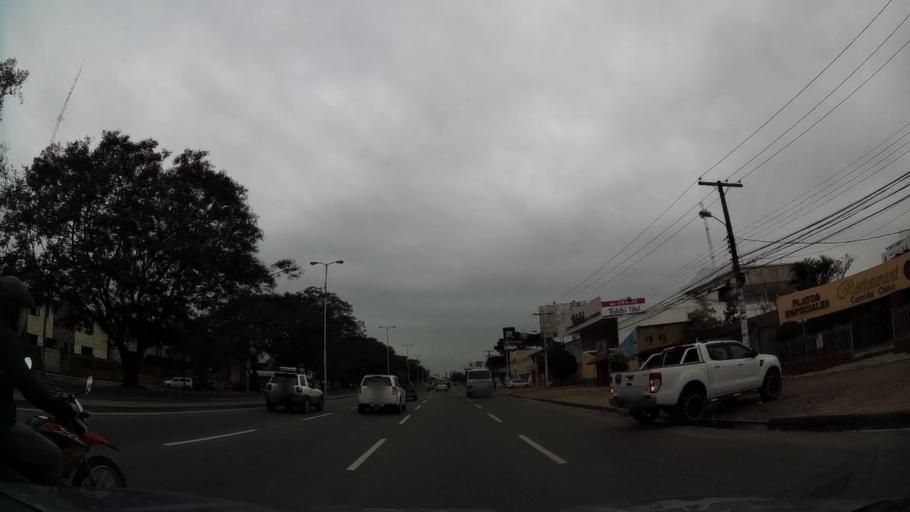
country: BO
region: Santa Cruz
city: Santa Cruz de la Sierra
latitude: -17.7702
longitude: -63.1748
